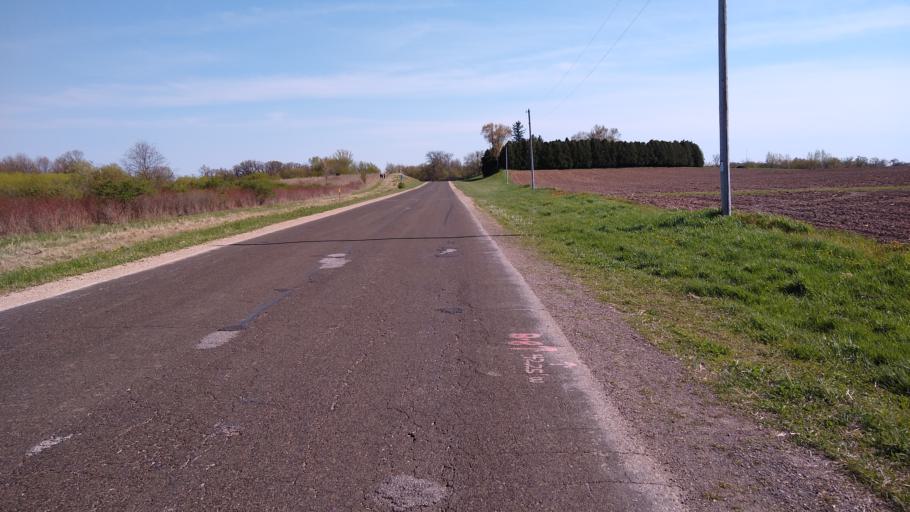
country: US
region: Wisconsin
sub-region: Dane County
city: Waunakee
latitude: 43.1450
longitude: -89.4385
